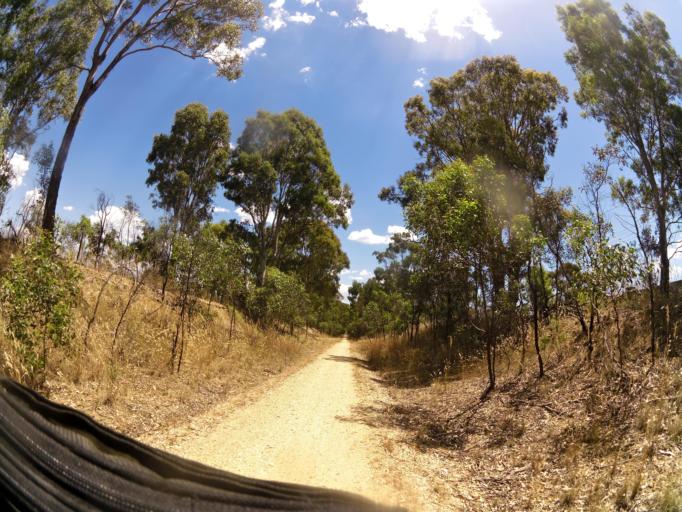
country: AU
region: Victoria
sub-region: Wellington
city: Heyfield
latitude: -37.9813
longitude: 146.8045
